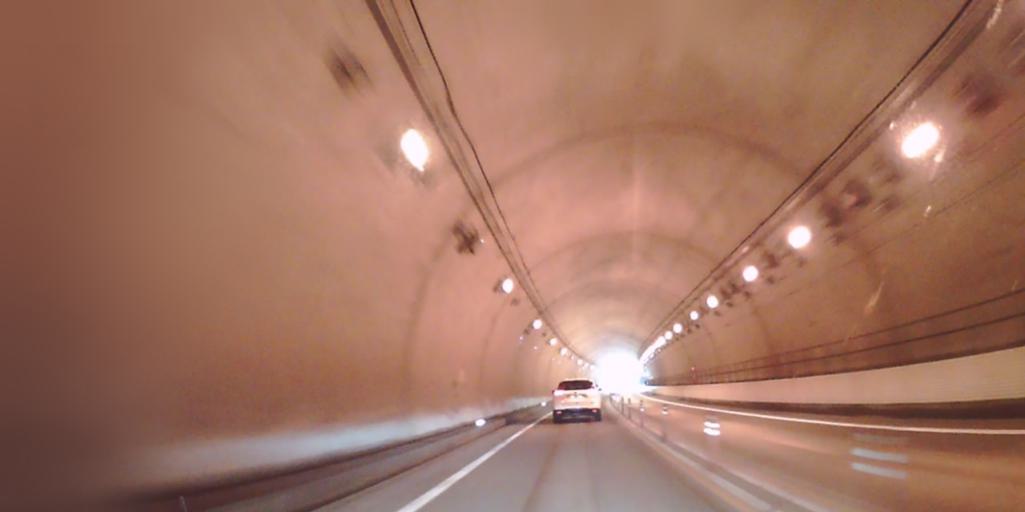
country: JP
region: Hokkaido
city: Date
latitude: 42.5591
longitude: 140.7640
